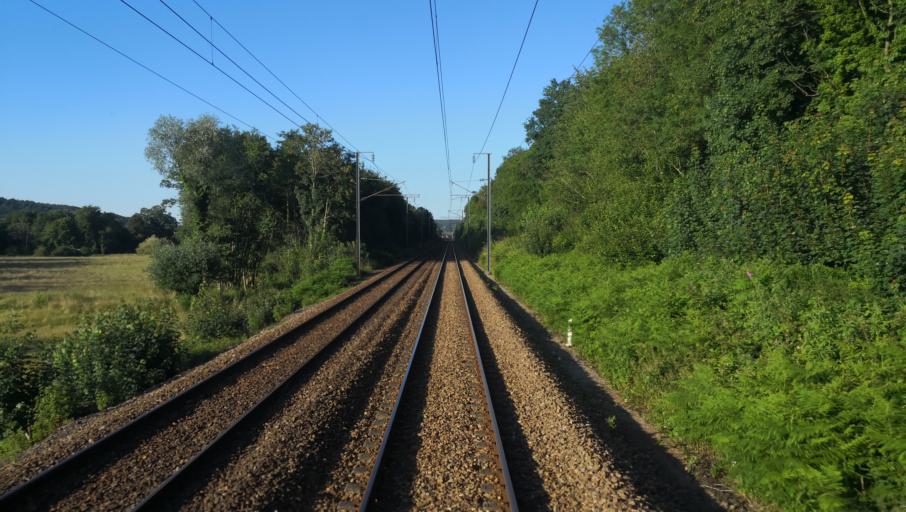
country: FR
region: Haute-Normandie
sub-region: Departement de l'Eure
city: Serquigny
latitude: 49.0990
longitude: 0.7029
